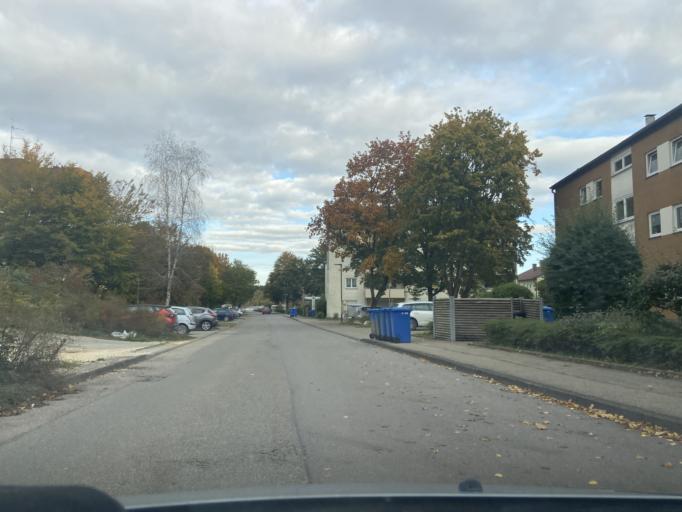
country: DE
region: Baden-Wuerttemberg
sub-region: Tuebingen Region
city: Sigmaringen
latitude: 48.0971
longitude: 9.2285
